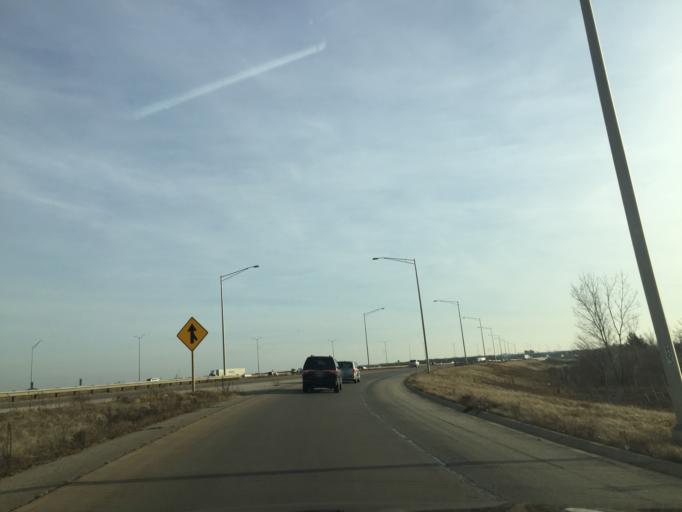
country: US
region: Illinois
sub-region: Will County
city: Bolingbrook
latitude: 41.7005
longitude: -88.0320
